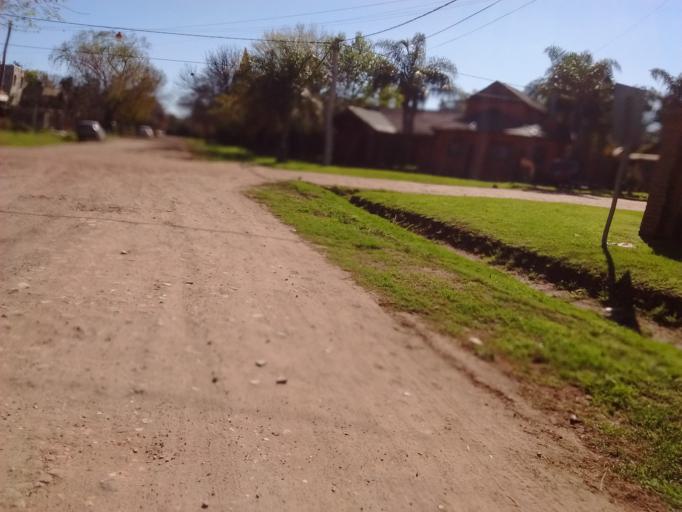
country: AR
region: Santa Fe
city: Funes
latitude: -32.9268
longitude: -60.8136
